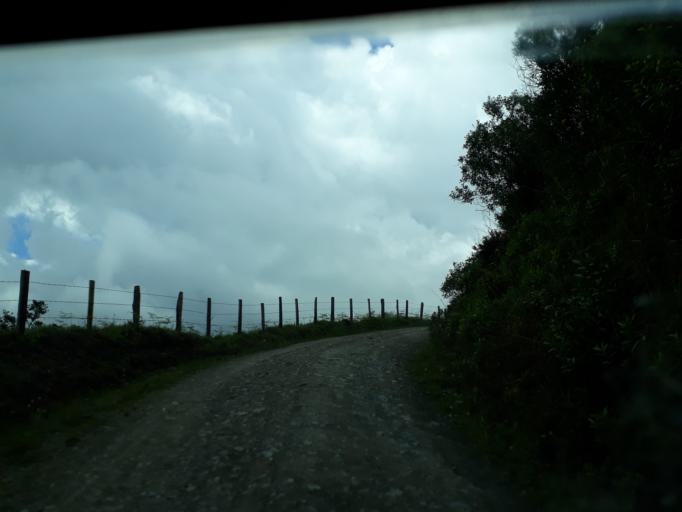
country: CO
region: Cundinamarca
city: Carmen de Carupa
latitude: 5.3758
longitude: -73.9861
